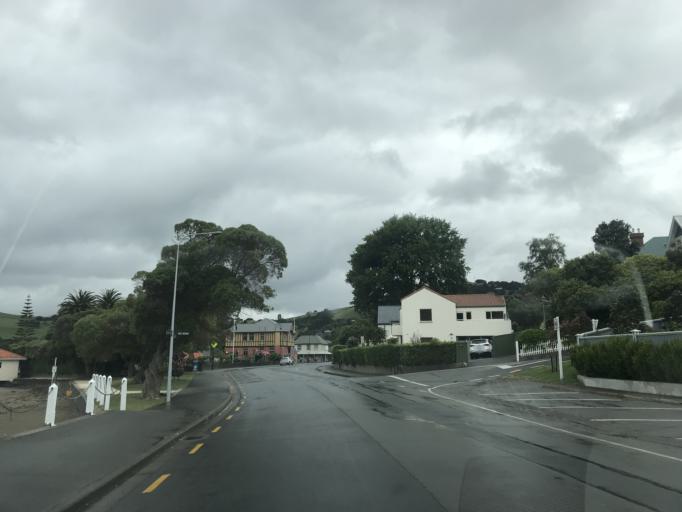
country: NZ
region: Canterbury
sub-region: Christchurch City
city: Christchurch
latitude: -43.8067
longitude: 172.9664
